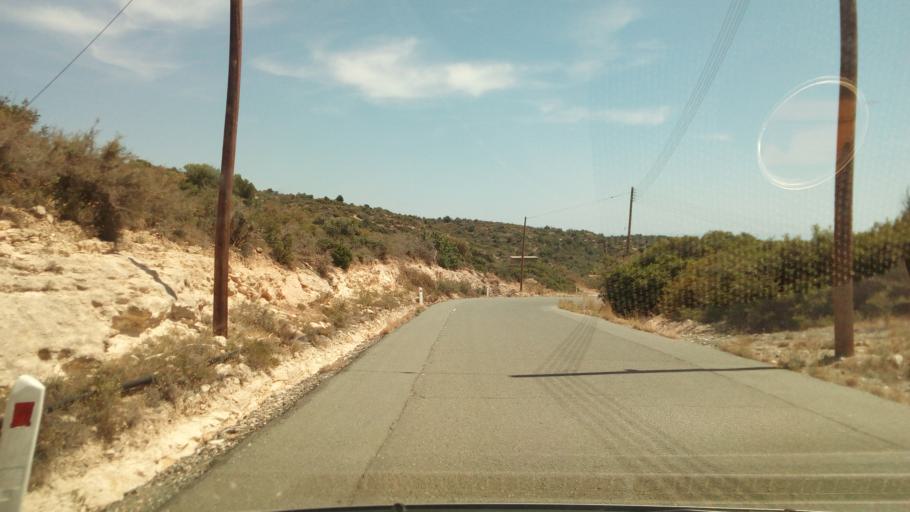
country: CY
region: Limassol
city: Pissouri
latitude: 34.7212
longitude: 32.6025
